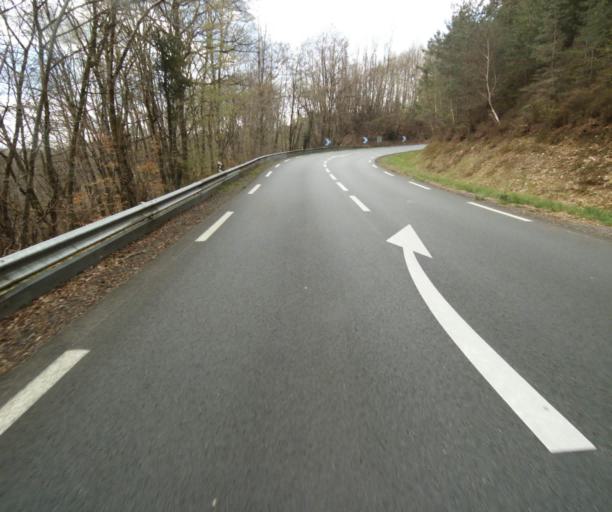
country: FR
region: Limousin
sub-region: Departement de la Correze
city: Sainte-Fortunade
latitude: 45.1885
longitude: 1.8455
